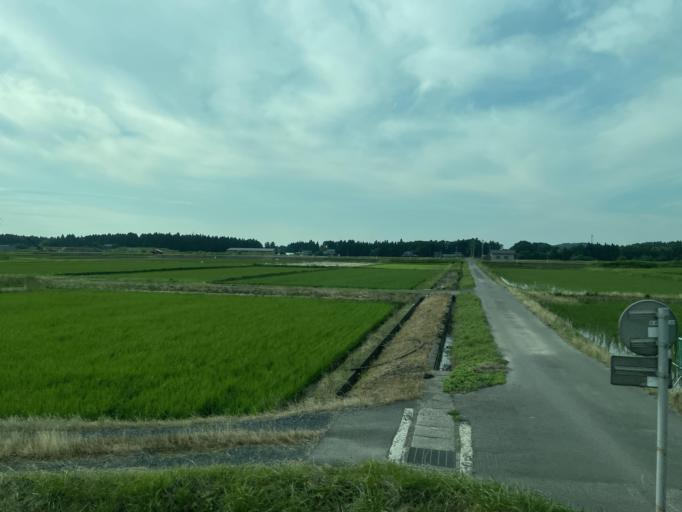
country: JP
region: Niigata
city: Gosen
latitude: 37.7360
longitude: 139.2524
